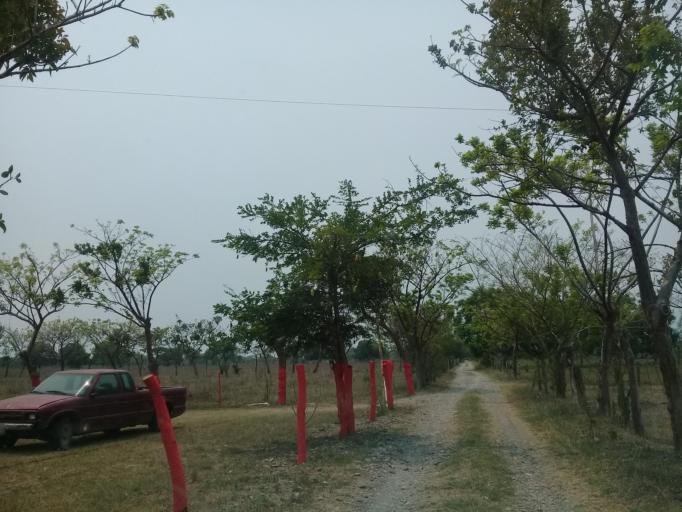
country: MX
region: Veracruz
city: Jamapa
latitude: 18.9300
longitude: -96.2040
